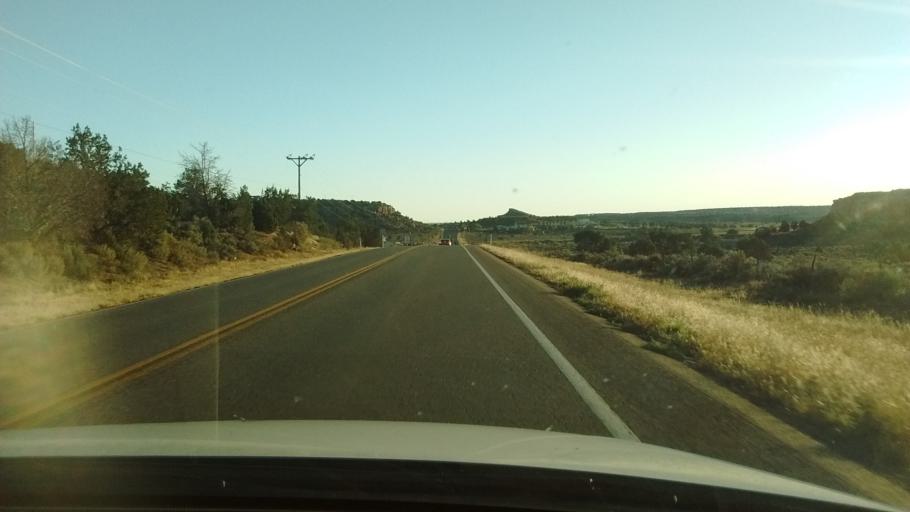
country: US
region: Utah
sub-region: Kane County
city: Kanab
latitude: 37.0028
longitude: -112.5296
